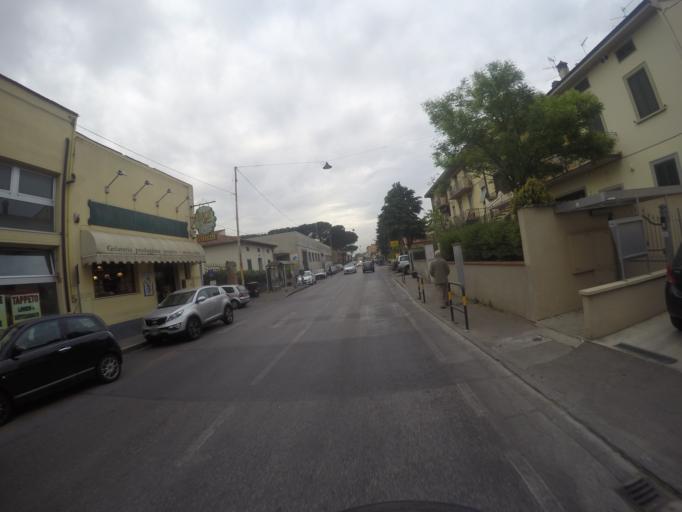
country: IT
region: Tuscany
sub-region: Provincia di Prato
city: Prato
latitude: 43.8927
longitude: 11.0708
